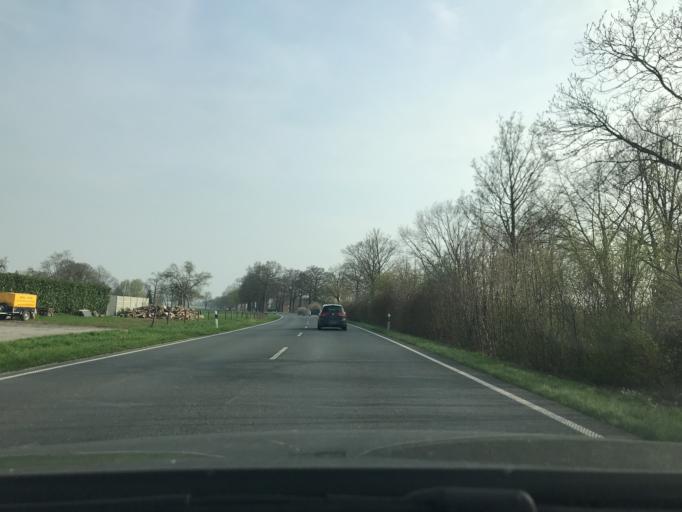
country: DE
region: North Rhine-Westphalia
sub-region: Regierungsbezirk Dusseldorf
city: Kevelaer
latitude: 51.5455
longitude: 6.2679
